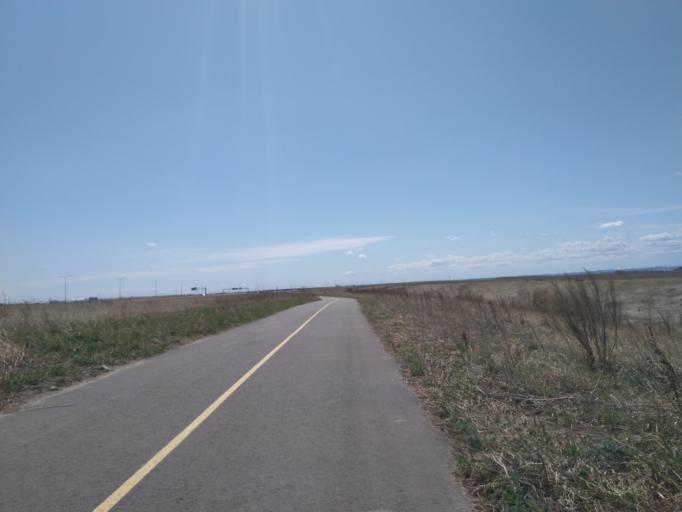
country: CA
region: Alberta
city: Chestermere
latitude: 51.0306
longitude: -113.9238
